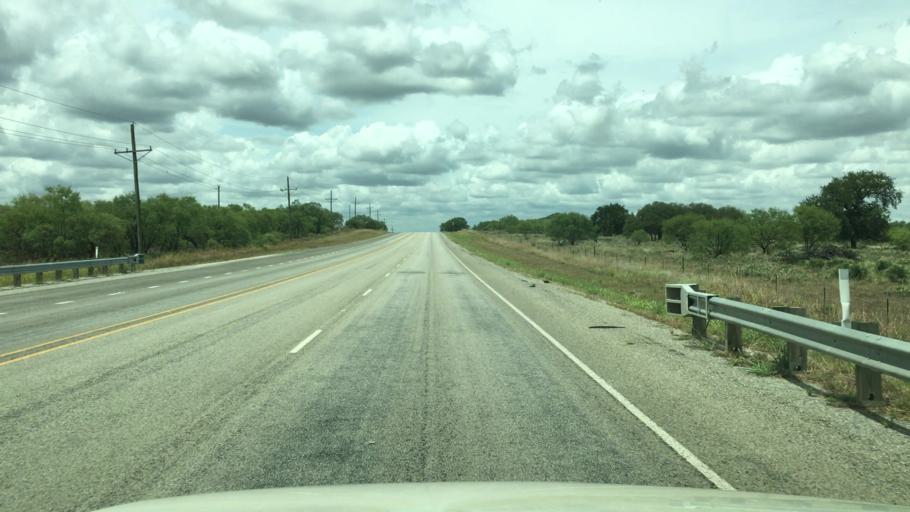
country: US
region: Texas
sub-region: McCulloch County
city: Brady
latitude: 31.0023
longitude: -99.1776
